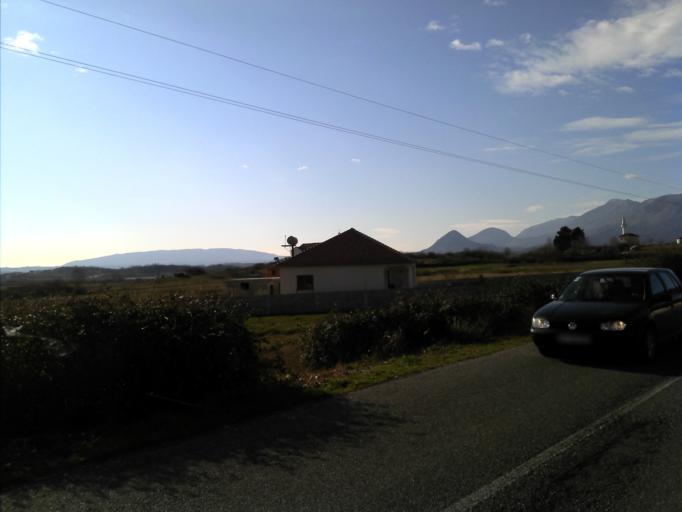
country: AL
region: Shkoder
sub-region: Rrethi i Shkodres
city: Dajc
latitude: 42.0149
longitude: 19.4012
